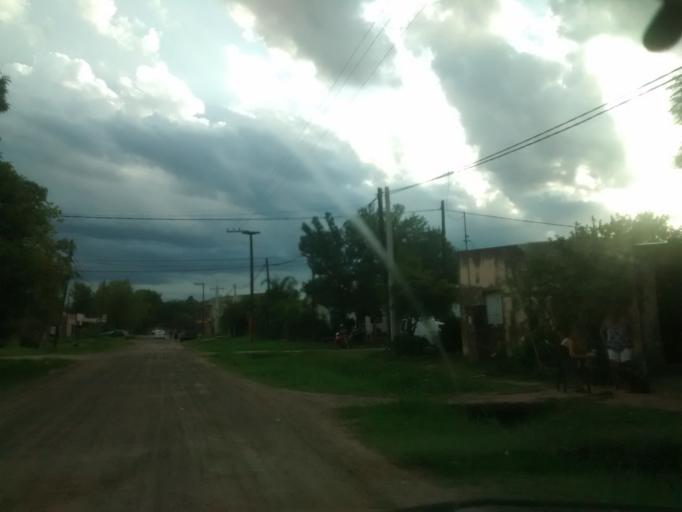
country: AR
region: Chaco
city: Fontana
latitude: -27.4286
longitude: -58.9953
